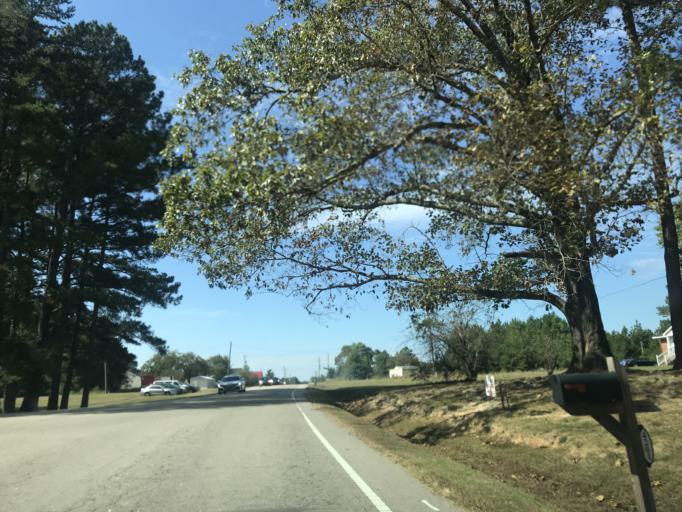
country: US
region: North Carolina
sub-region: Wake County
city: Rolesville
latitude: 35.8811
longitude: -78.5022
